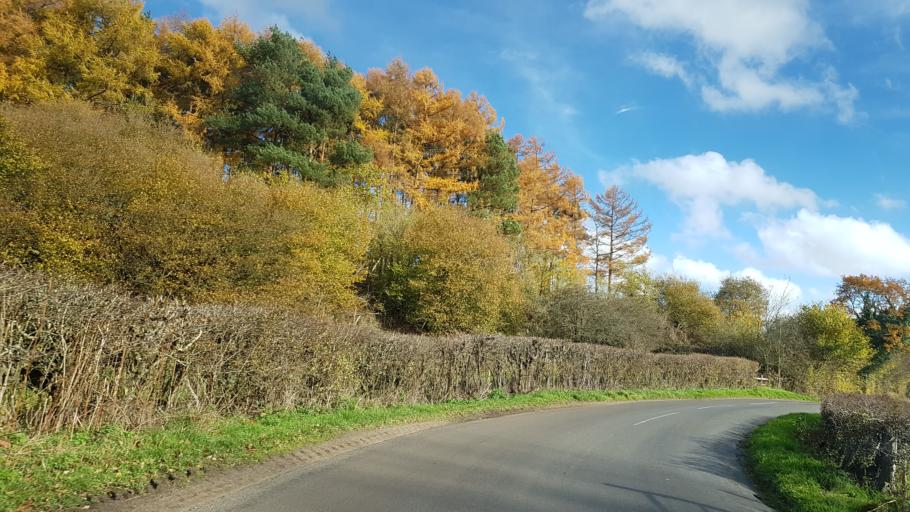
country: GB
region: England
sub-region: Surrey
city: Seale
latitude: 51.2220
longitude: -0.7014
